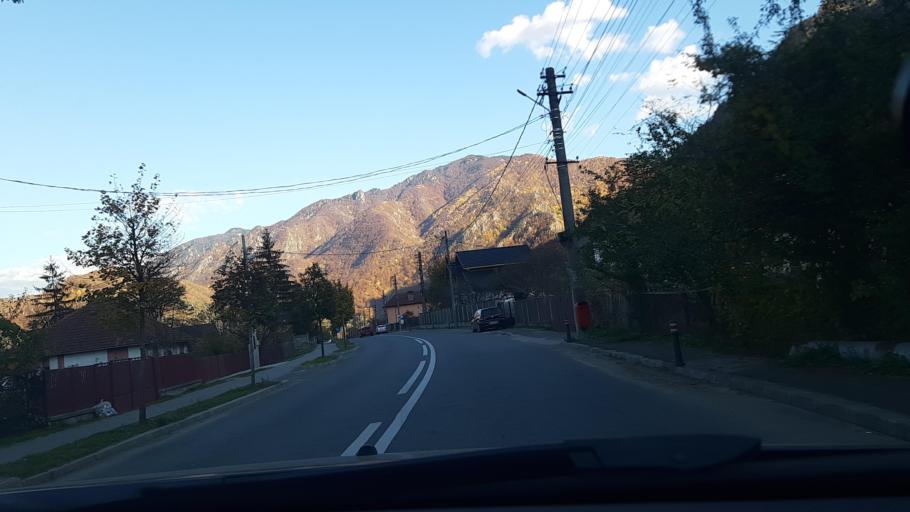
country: RO
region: Valcea
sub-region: Comuna Brezoi
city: Brezoi
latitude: 45.3334
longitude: 24.2572
